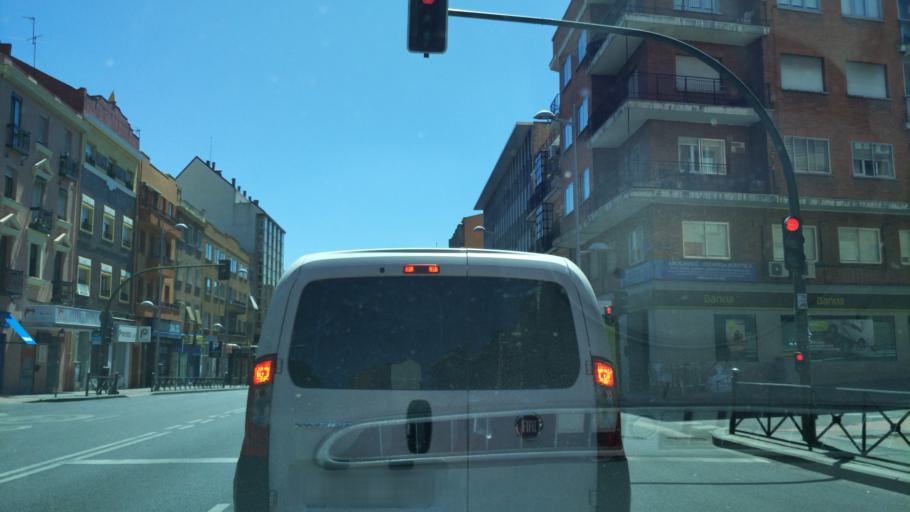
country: ES
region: Madrid
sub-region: Provincia de Madrid
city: Chamartin
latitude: 40.4639
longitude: -3.6962
